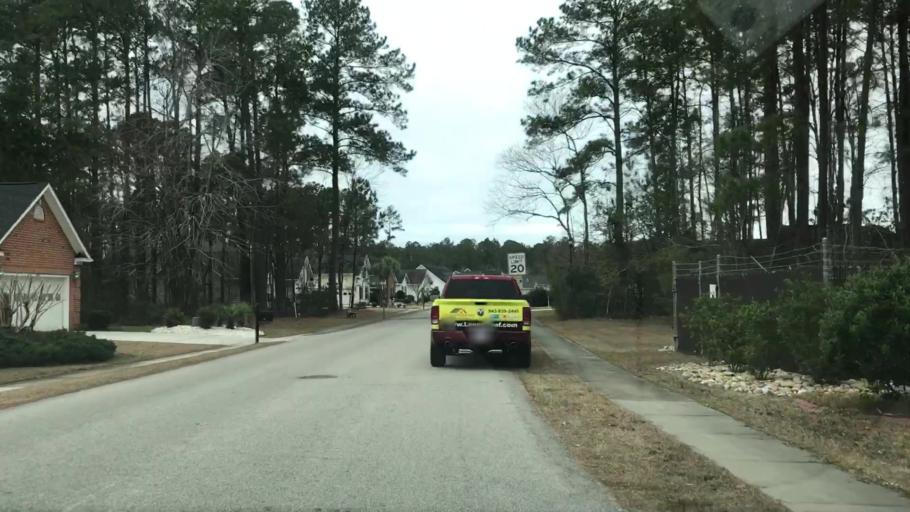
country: US
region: South Carolina
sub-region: Horry County
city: Red Hill
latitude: 33.7718
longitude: -79.0062
